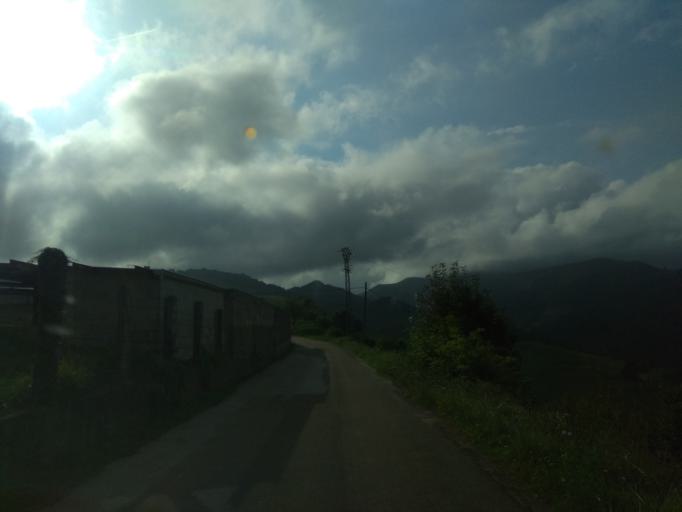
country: ES
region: Cantabria
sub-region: Provincia de Cantabria
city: San Vicente de la Barquera
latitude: 43.3117
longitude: -4.3887
